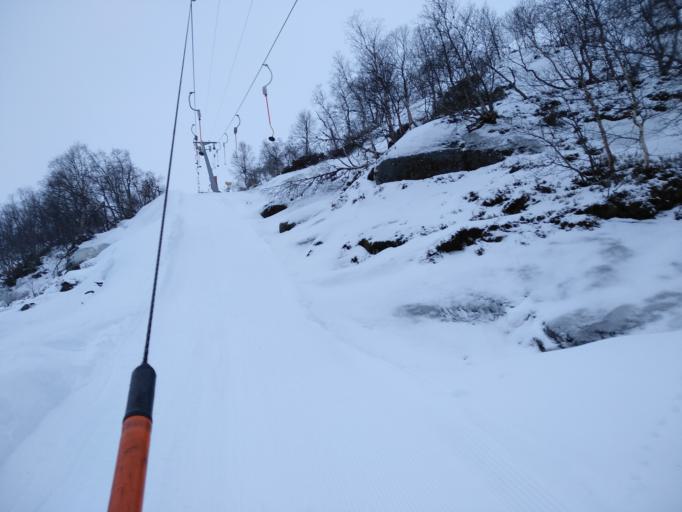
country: NO
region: Vest-Agder
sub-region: Sirdal
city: Tonstad
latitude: 59.0232
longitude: 6.9166
